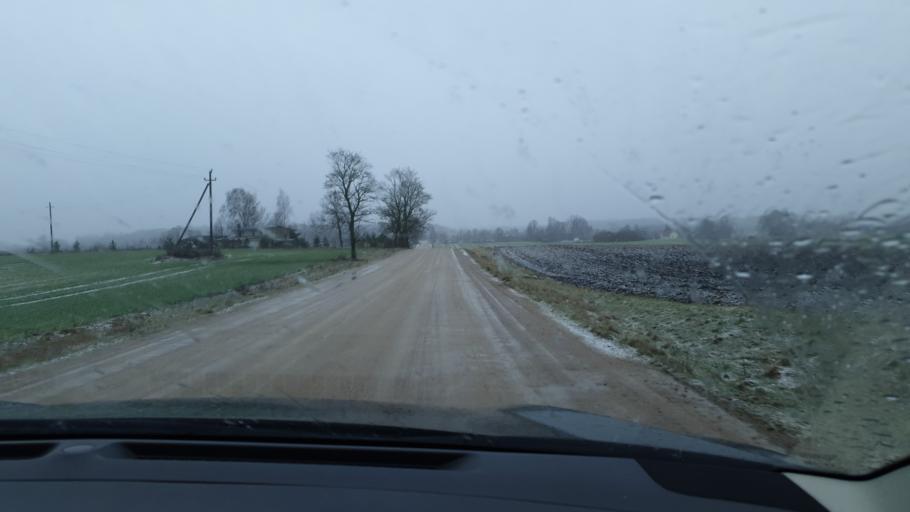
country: LT
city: Jieznas
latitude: 54.5793
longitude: 24.3168
